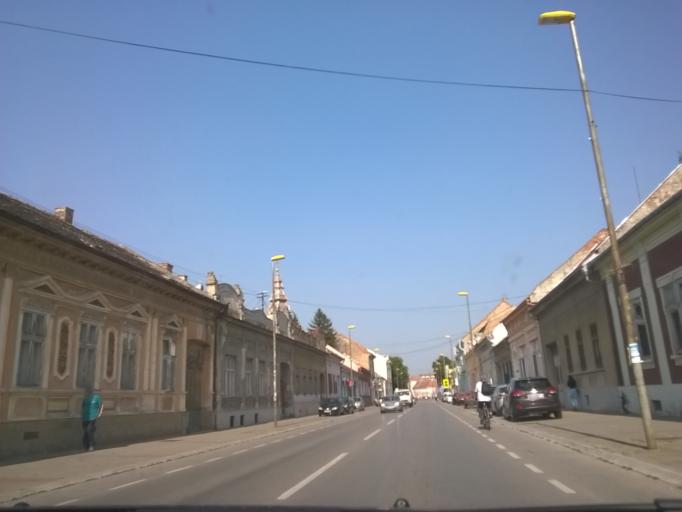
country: RS
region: Autonomna Pokrajina Vojvodina
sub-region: Juznobanatski Okrug
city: Vrsac
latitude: 45.1178
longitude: 21.2938
